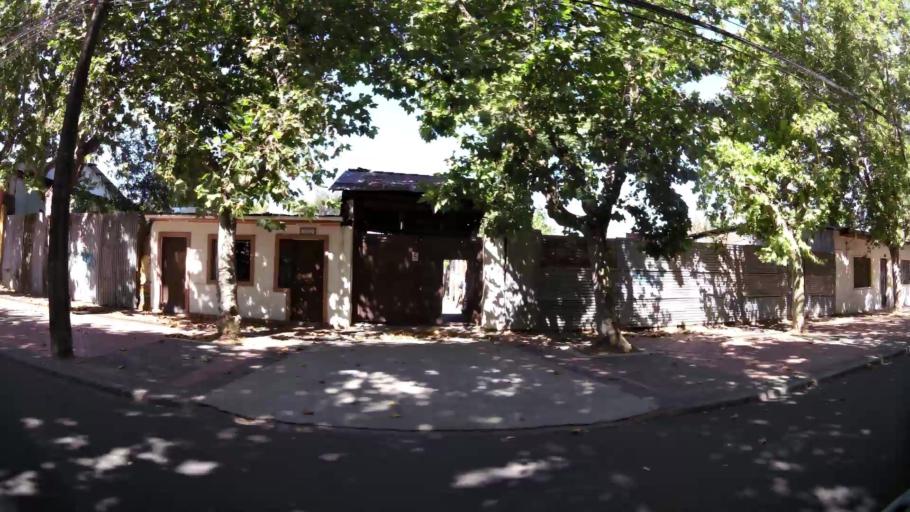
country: CL
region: Maule
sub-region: Provincia de Talca
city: Talca
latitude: -35.4204
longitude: -71.6579
